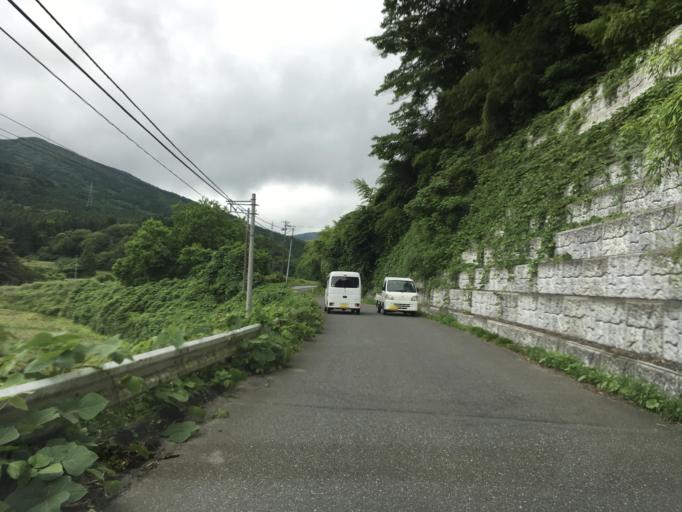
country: JP
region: Iwate
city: Ofunato
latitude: 38.8915
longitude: 141.4828
